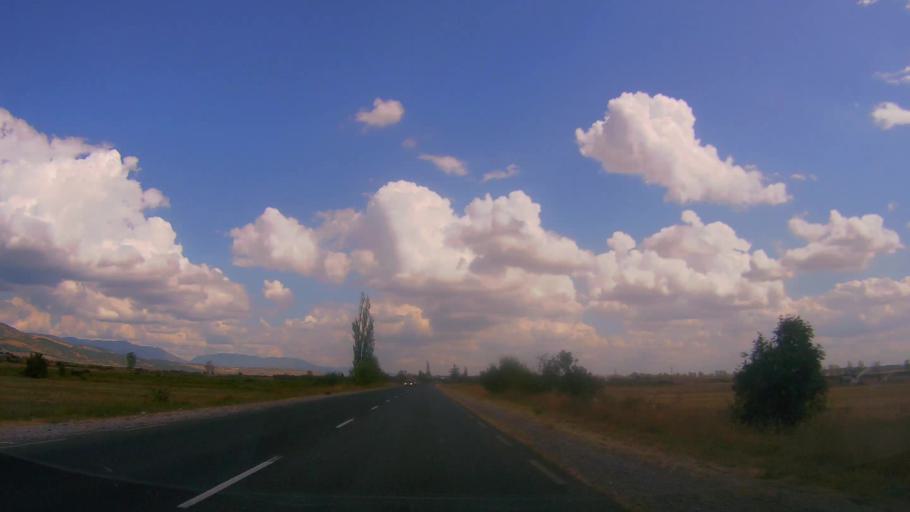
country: BG
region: Sliven
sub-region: Obshtina Sliven
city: Sliven
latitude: 42.6363
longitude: 26.2260
